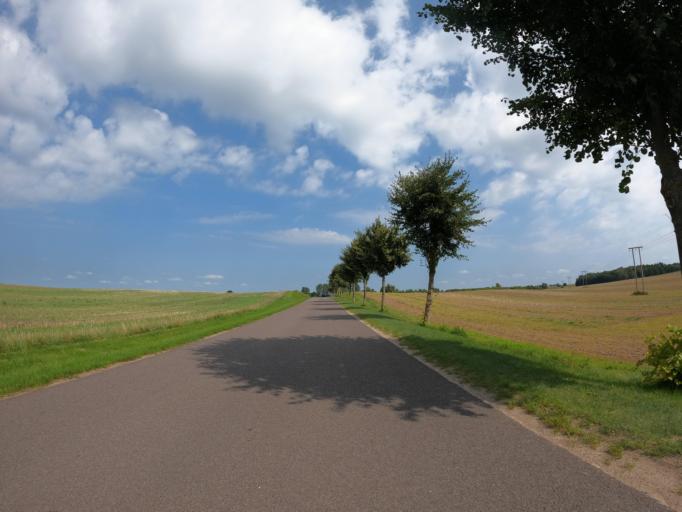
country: DE
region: Mecklenburg-Vorpommern
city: Malchow
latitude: 53.4555
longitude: 12.4740
